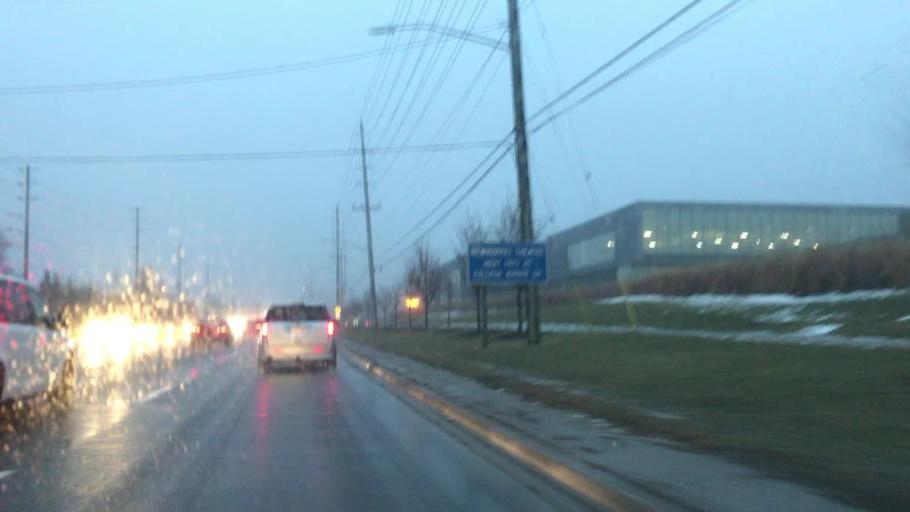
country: CA
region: Ontario
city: Newmarket
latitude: 44.0445
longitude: -79.4404
